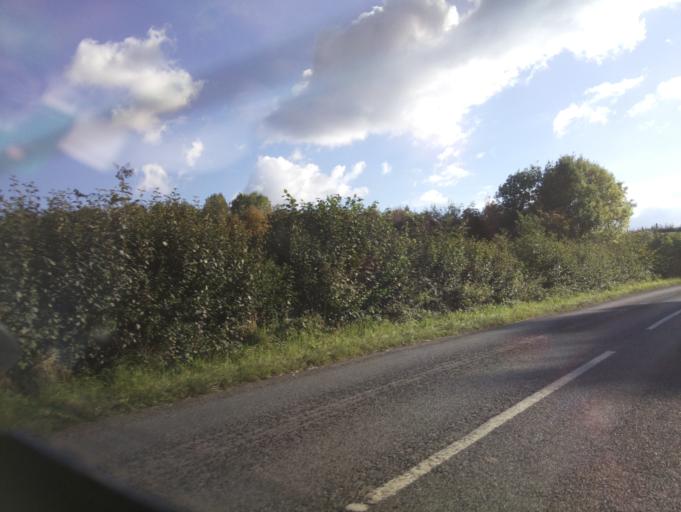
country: GB
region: England
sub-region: Herefordshire
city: Clifford
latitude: 52.1106
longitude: -3.0960
